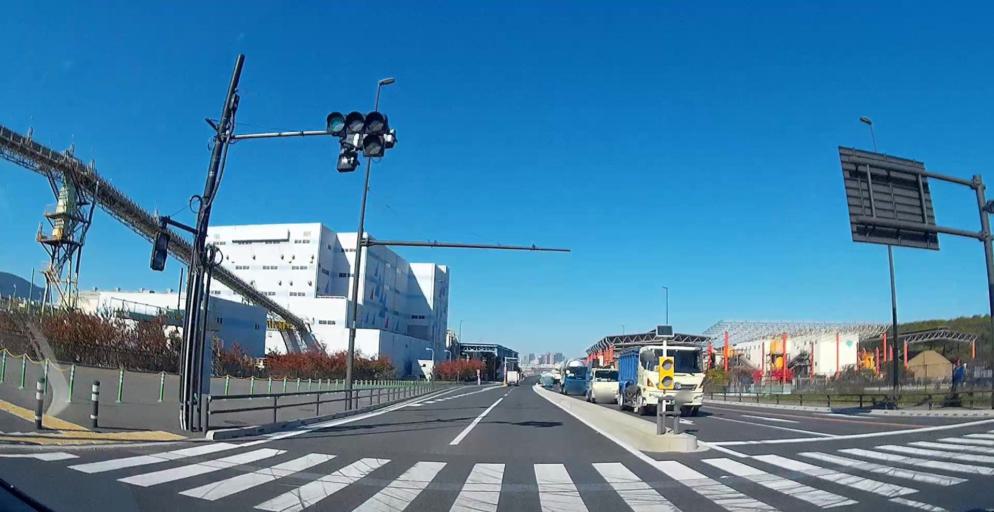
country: JP
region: Tokyo
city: Urayasu
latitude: 35.6015
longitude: 139.8043
